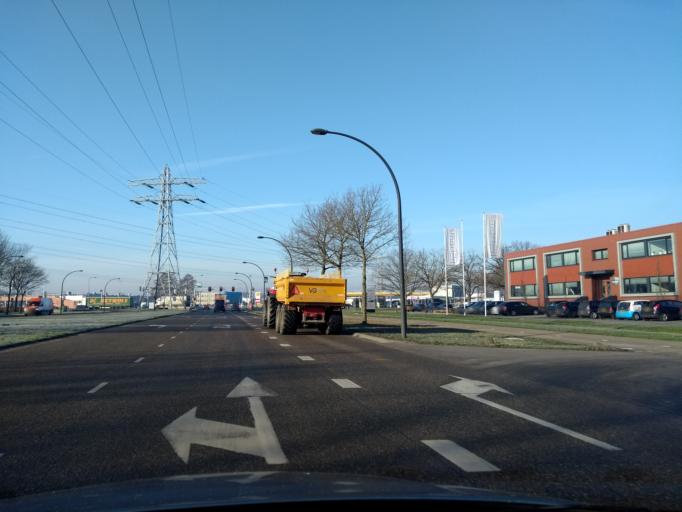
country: NL
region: Overijssel
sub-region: Gemeente Hengelo
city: Hengelo
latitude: 52.2423
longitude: 6.7677
